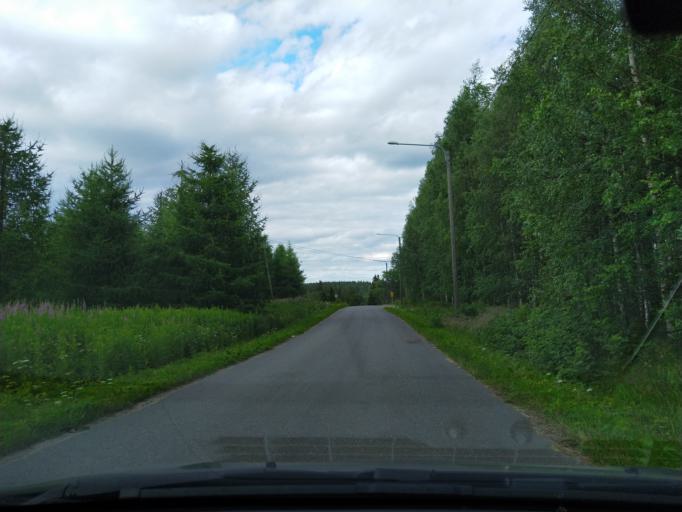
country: FI
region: Kymenlaakso
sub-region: Kouvola
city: Kouvola
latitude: 61.0469
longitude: 26.8439
